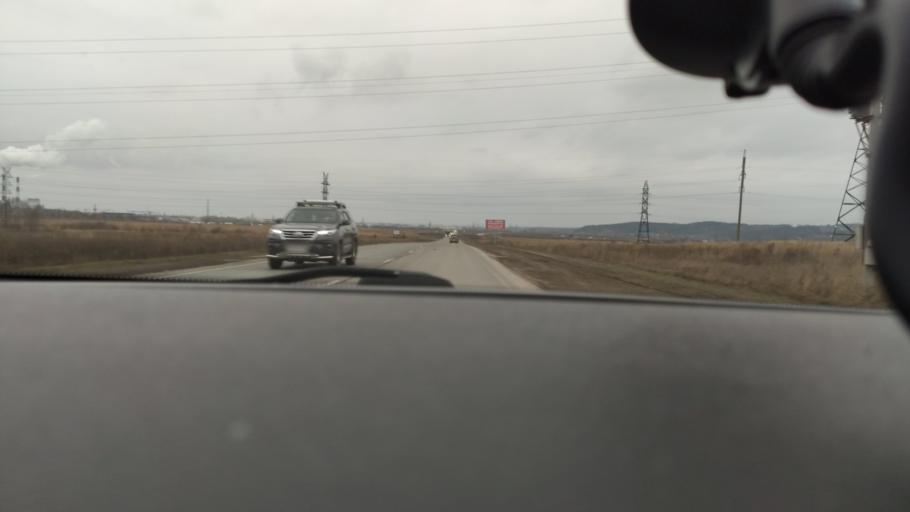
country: RU
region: Perm
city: Froly
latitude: 57.9170
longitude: 56.1845
